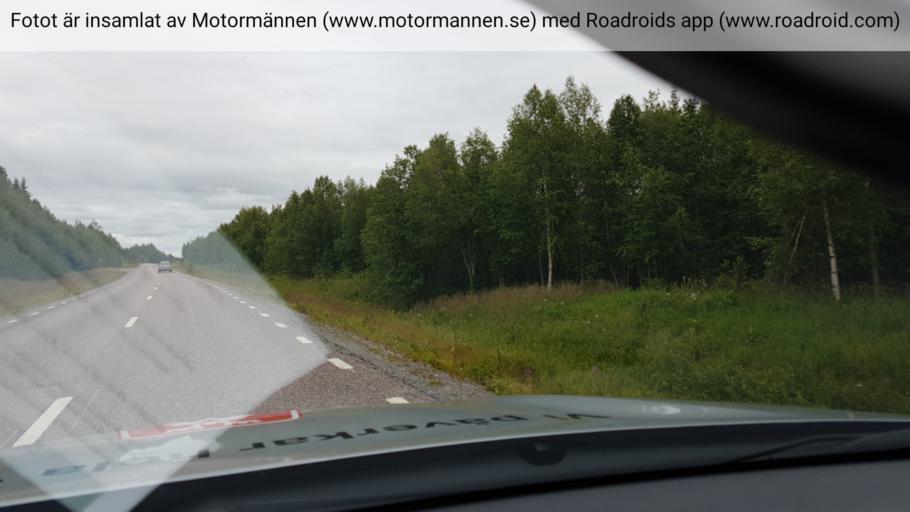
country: SE
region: Norrbotten
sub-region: Gallivare Kommun
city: Gaellivare
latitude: 67.0300
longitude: 21.7352
